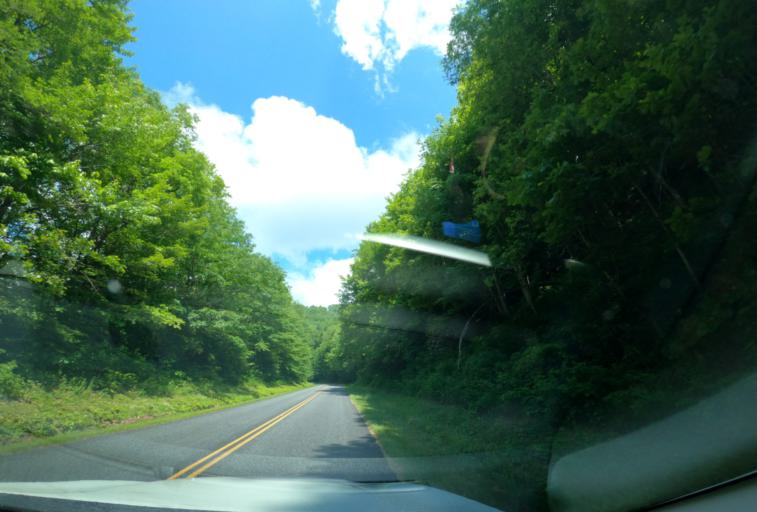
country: US
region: North Carolina
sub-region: Haywood County
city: Maggie Valley
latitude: 35.4496
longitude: -83.1095
